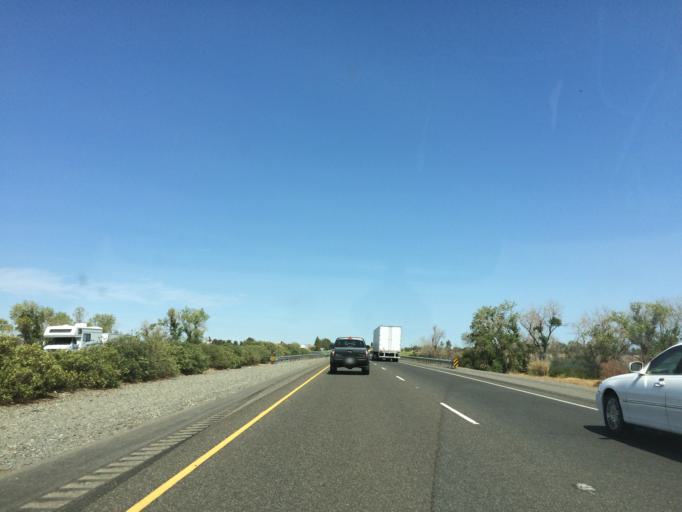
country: US
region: California
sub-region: Glenn County
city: Orland
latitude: 39.7685
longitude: -122.2049
